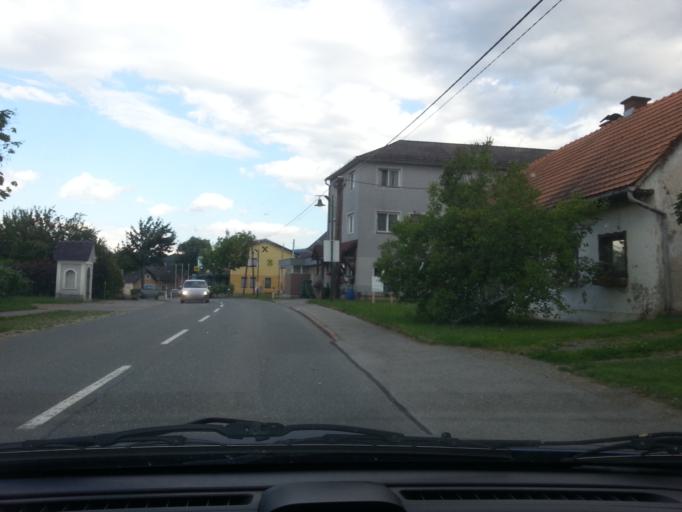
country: AT
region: Styria
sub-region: Politischer Bezirk Leibnitz
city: Oberhaag
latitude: 46.6848
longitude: 15.3381
